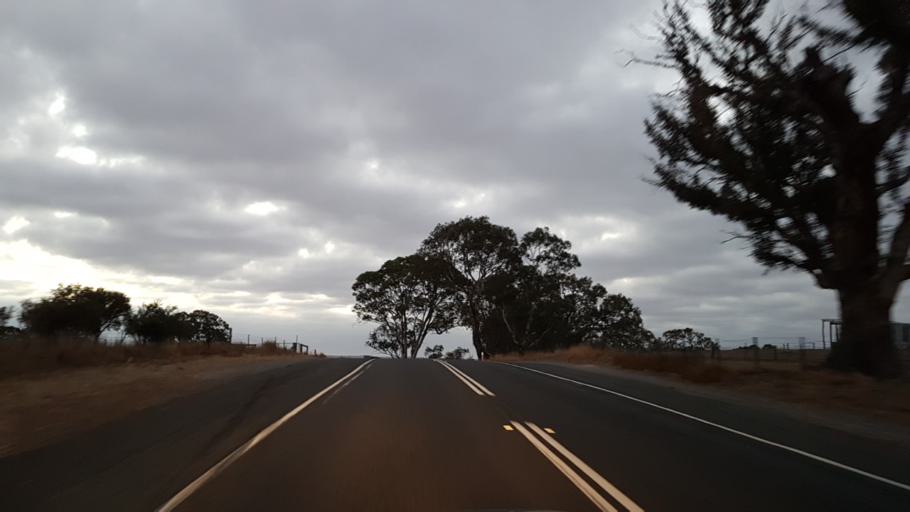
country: AU
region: South Australia
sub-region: Mount Barker
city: Nairne
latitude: -35.0300
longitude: 138.9597
